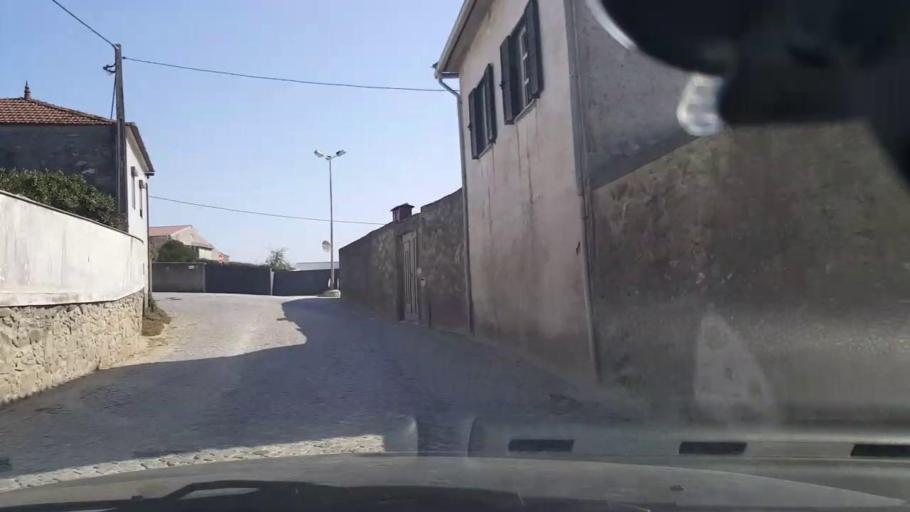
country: PT
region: Porto
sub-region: Povoa de Varzim
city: Pedroso
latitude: 41.4014
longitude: -8.6860
